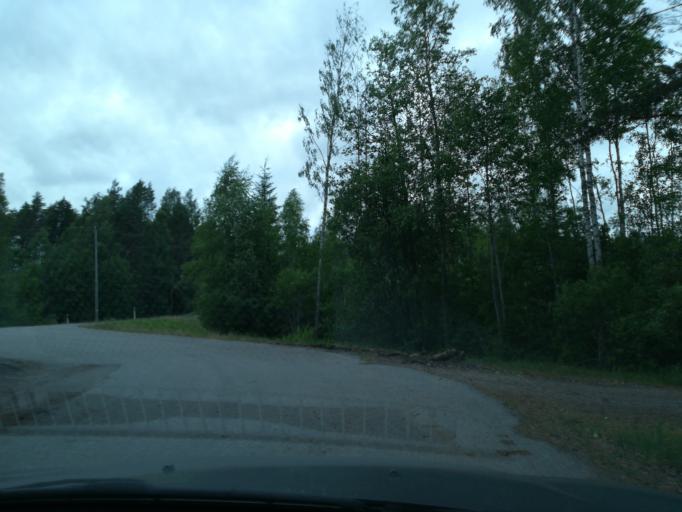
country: FI
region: Southern Savonia
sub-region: Mikkeli
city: Ristiina
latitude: 61.2752
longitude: 27.4078
